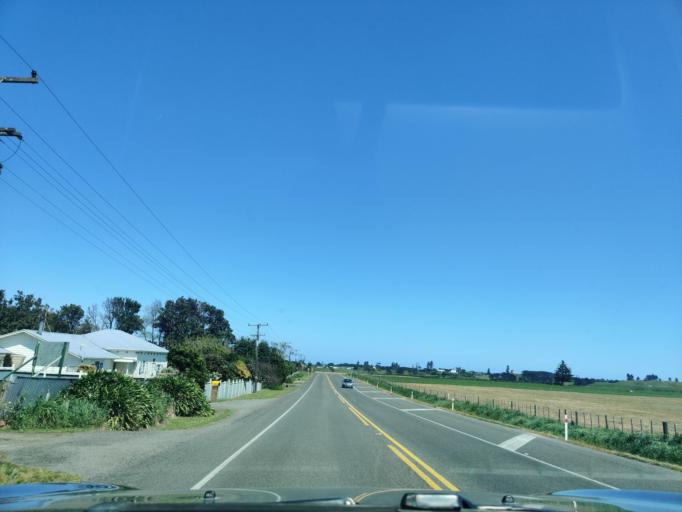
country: NZ
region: Taranaki
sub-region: South Taranaki District
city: Patea
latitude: -39.7450
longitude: 174.4897
